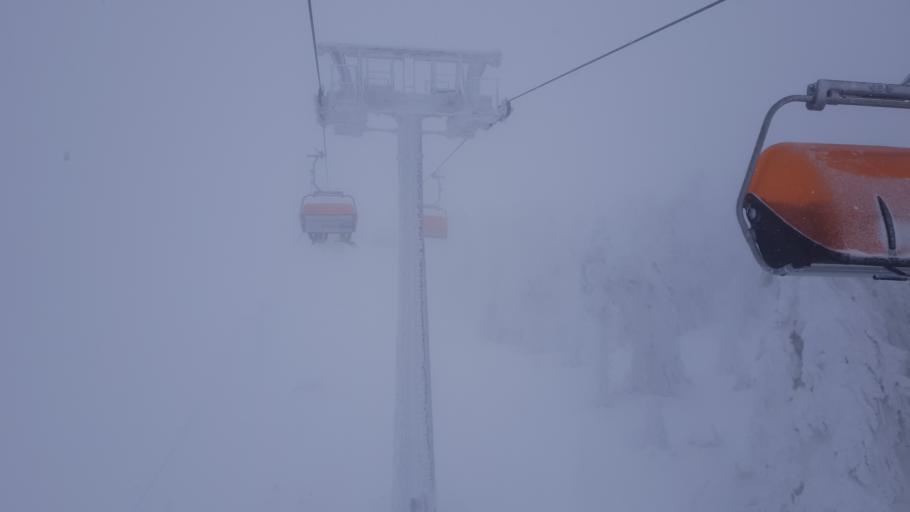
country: DE
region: Saxony
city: Kurort Oberwiesenthal
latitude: 50.3932
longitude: 12.9645
